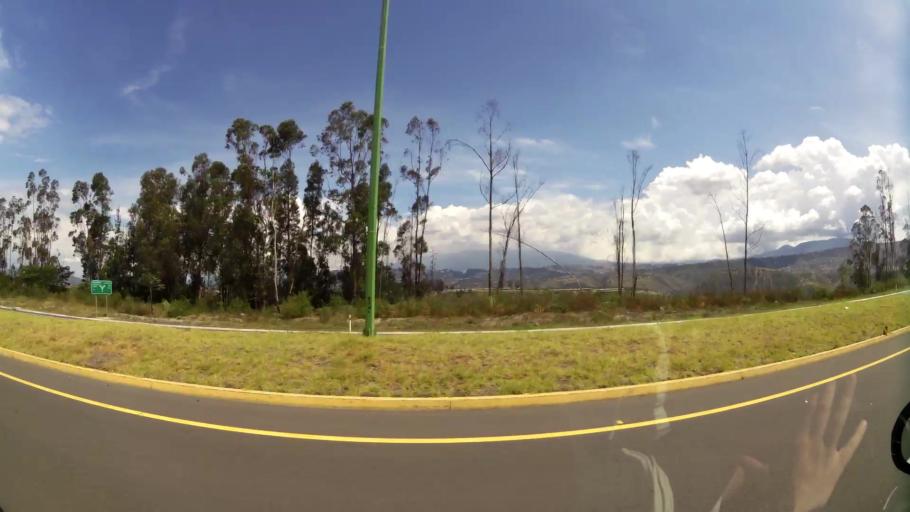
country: EC
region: Pichincha
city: Quito
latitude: -0.1328
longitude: -78.3597
